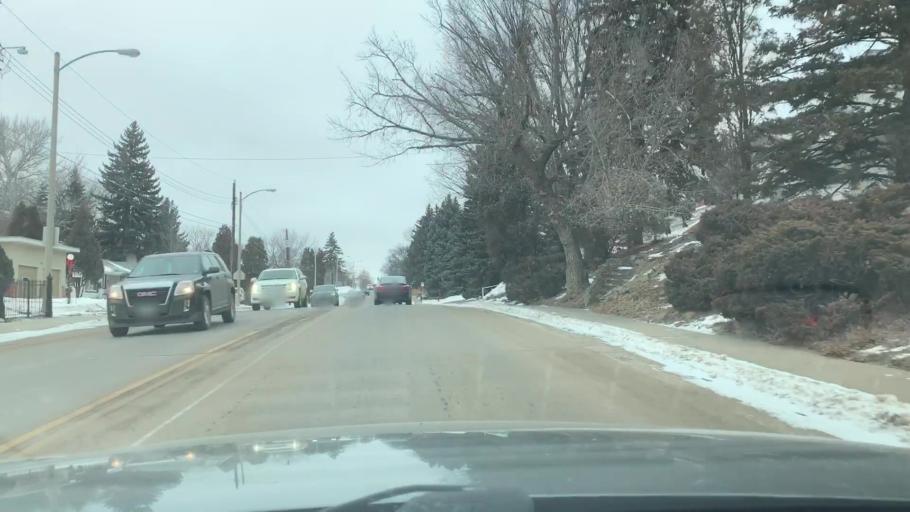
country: US
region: North Dakota
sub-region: Burleigh County
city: Bismarck
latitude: 46.8141
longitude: -100.7942
